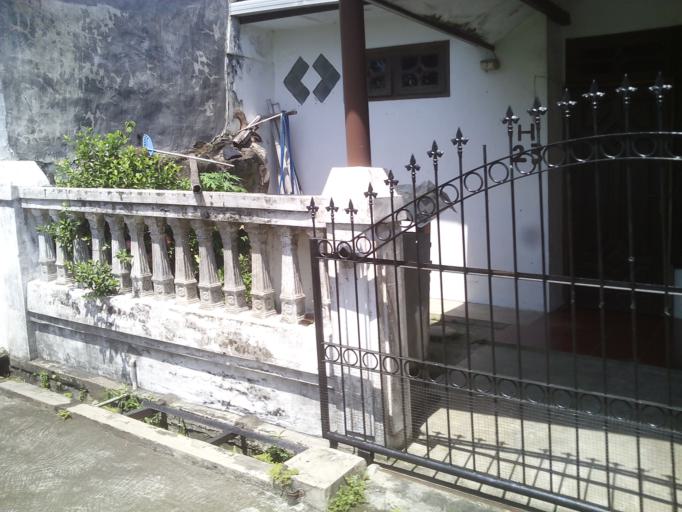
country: ID
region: East Java
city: Sumbersari Wetan
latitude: -8.1796
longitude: 113.7191
